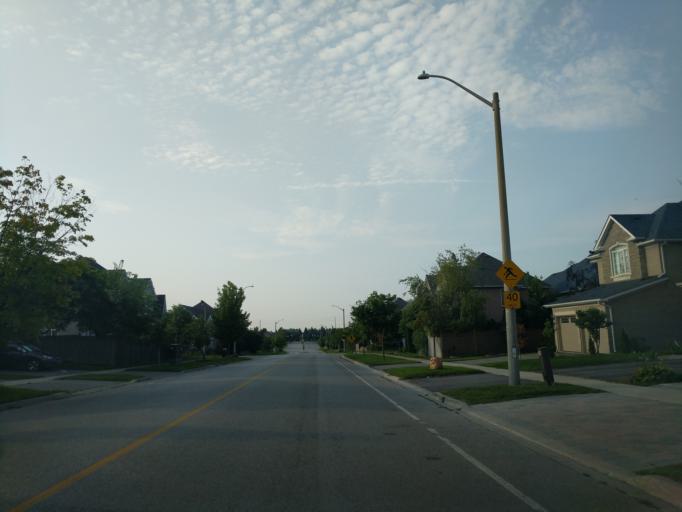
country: CA
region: Ontario
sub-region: York
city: Richmond Hill
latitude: 43.8802
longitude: -79.4078
